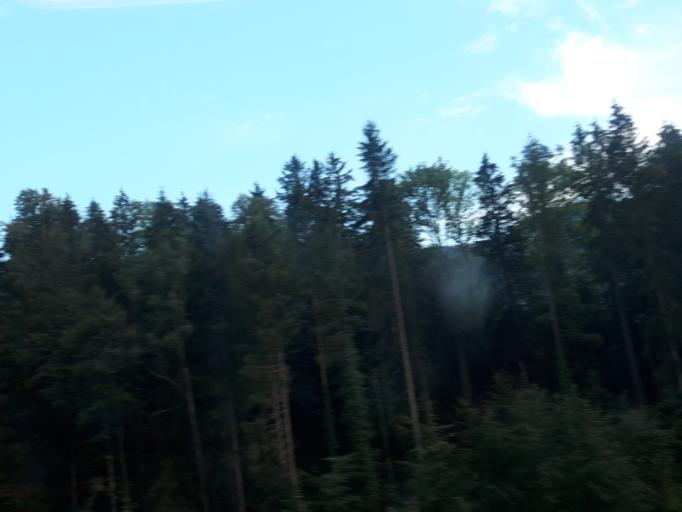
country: CH
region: Bern
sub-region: Jura bernois
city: Moutier
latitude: 47.2804
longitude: 7.4080
